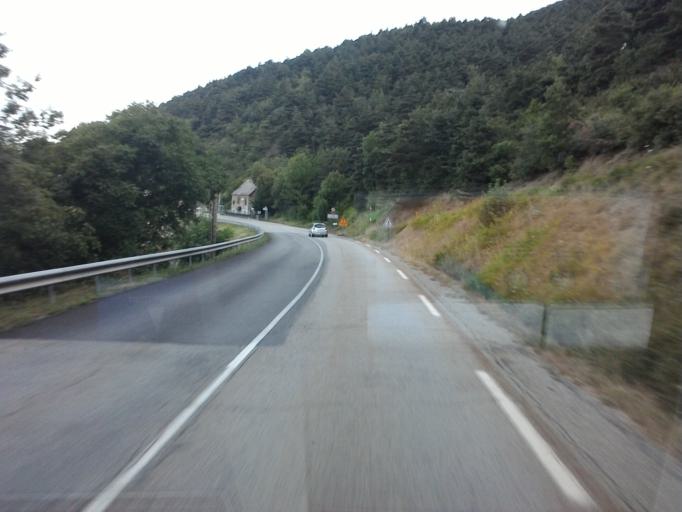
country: FR
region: Rhone-Alpes
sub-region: Departement de l'Isere
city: La Mure
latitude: 44.8397
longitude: 5.8770
